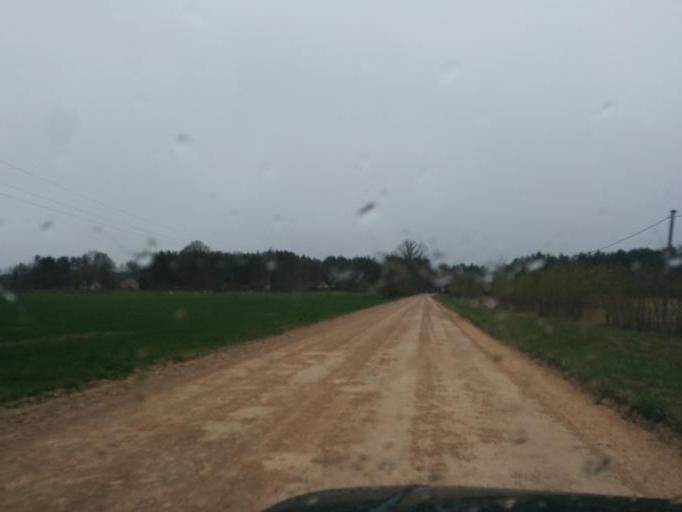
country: LV
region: Lecava
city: Iecava
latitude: 56.6136
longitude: 24.1770
